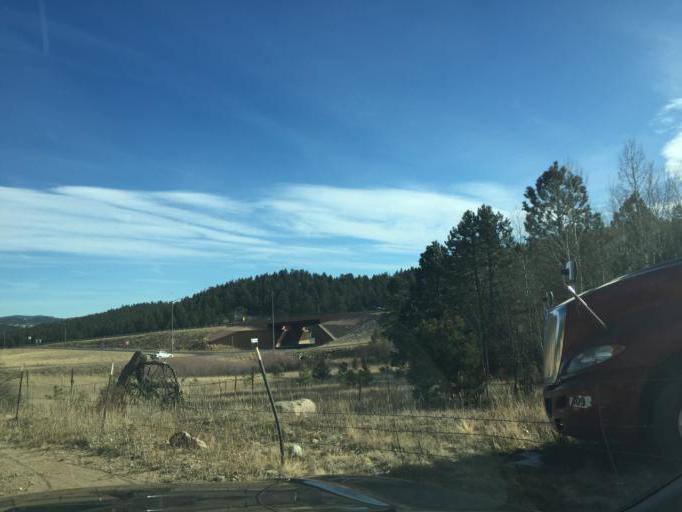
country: US
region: Colorado
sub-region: Jefferson County
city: Evergreen
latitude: 39.4359
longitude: -105.4631
